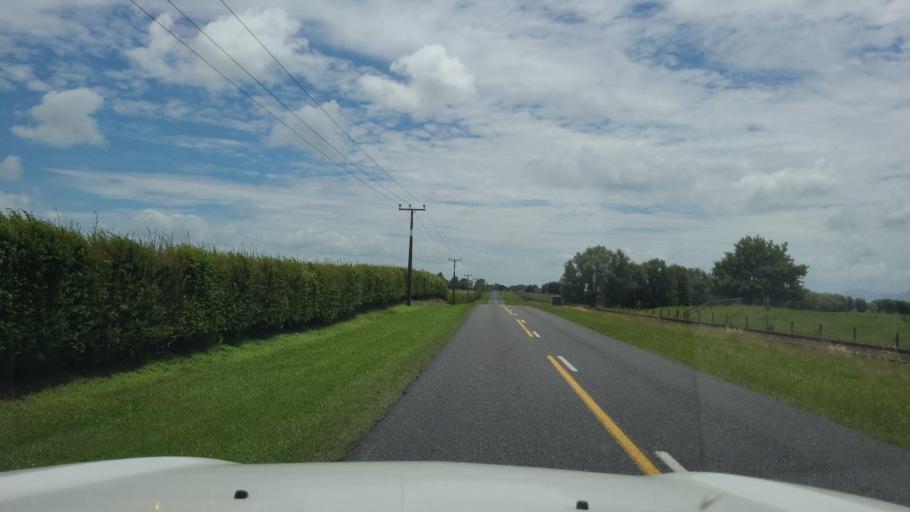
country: NZ
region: Waikato
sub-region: Matamata-Piako District
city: Matamata
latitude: -37.8745
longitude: 175.7575
